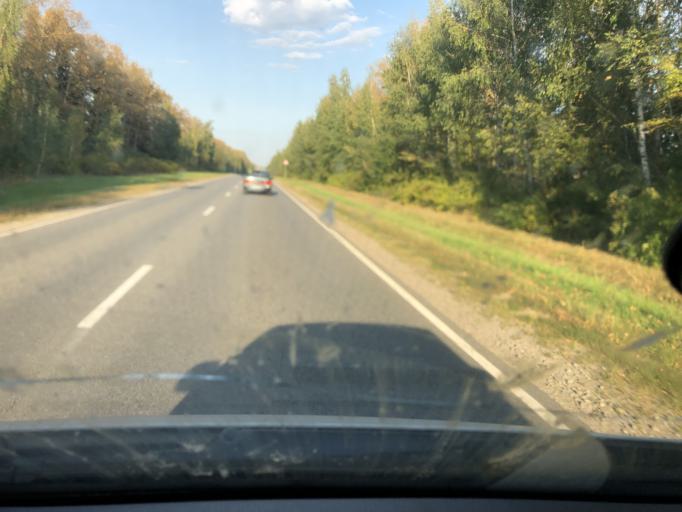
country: RU
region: Kaluga
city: Peremyshl'
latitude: 54.2442
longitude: 36.0838
